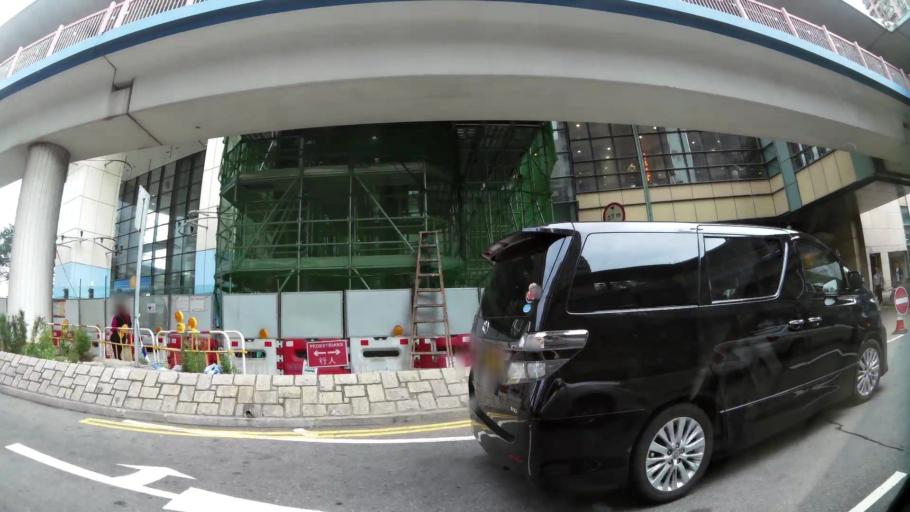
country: HK
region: Wanchai
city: Wan Chai
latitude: 22.2661
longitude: 114.2499
